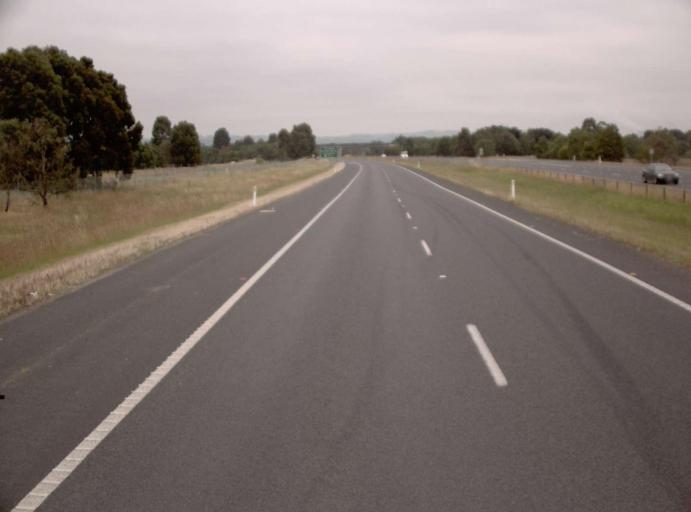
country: AU
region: Victoria
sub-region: Latrobe
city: Morwell
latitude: -38.2382
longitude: 146.3816
